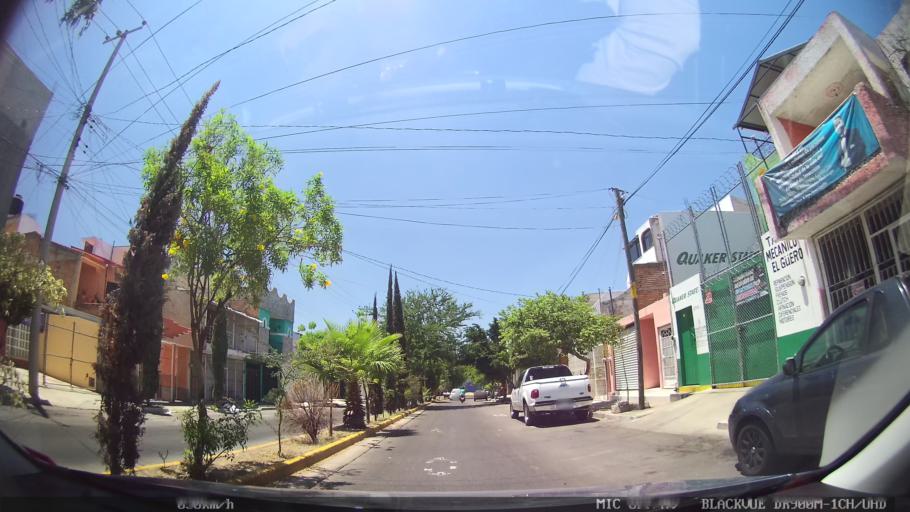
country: MX
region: Jalisco
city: Tlaquepaque
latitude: 20.6848
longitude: -103.2787
